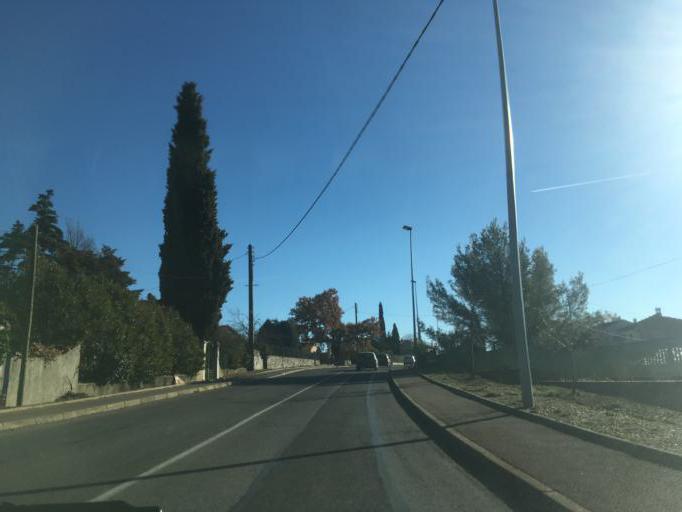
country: FR
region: Provence-Alpes-Cote d'Azur
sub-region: Departement du Var
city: Flayosc
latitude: 43.5380
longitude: 6.3875
